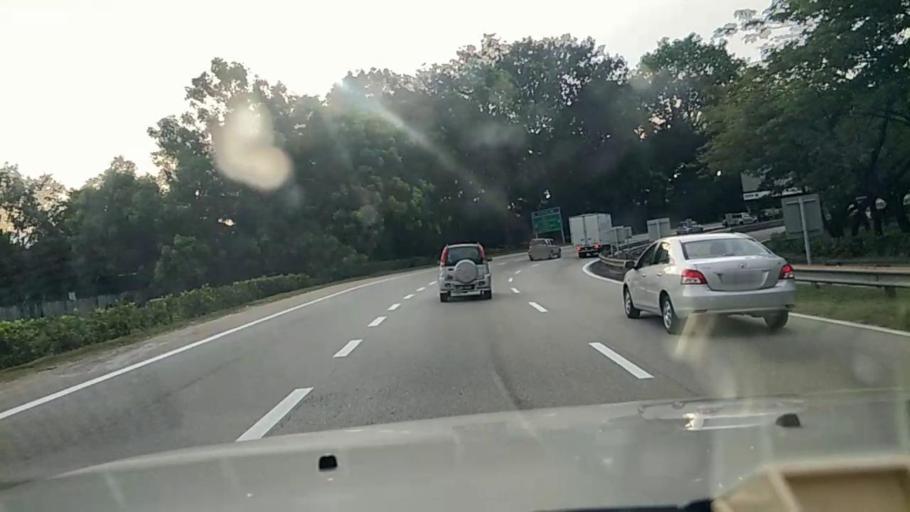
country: MY
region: Selangor
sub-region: Petaling
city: Petaling Jaya
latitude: 3.0987
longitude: 101.5881
